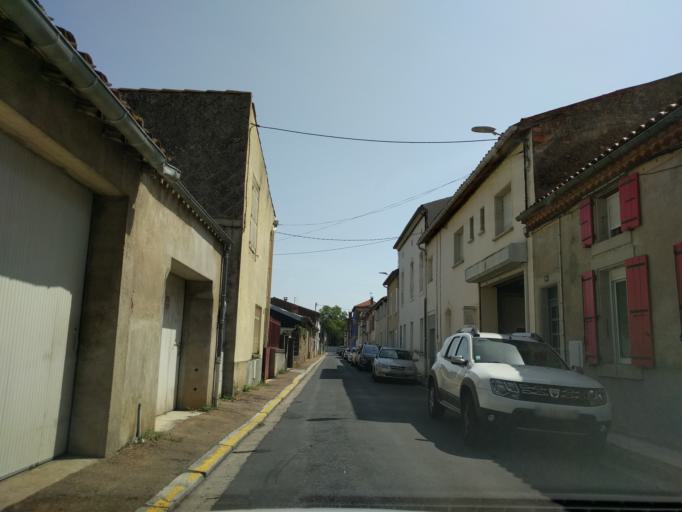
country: FR
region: Midi-Pyrenees
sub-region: Departement du Tarn
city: Castres
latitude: 43.5999
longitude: 2.2538
